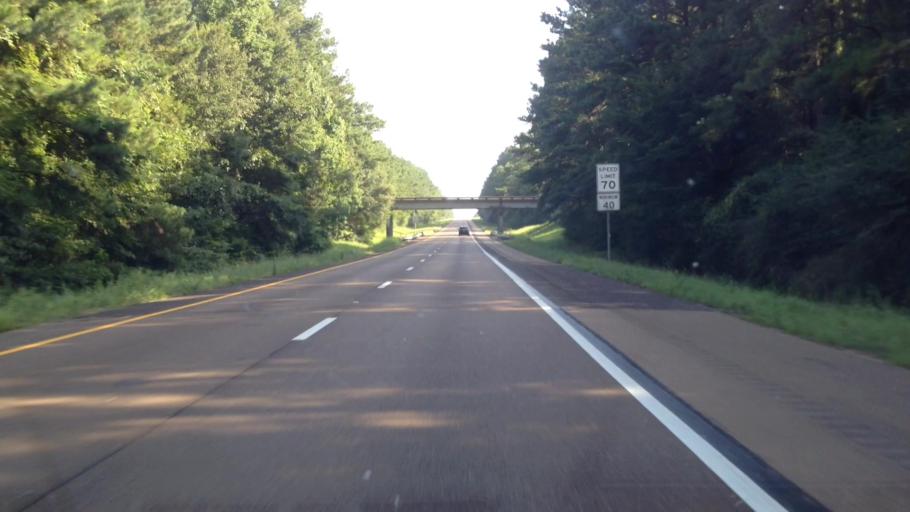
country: US
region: Mississippi
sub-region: Pike County
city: Summit
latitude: 31.3586
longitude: -90.4791
